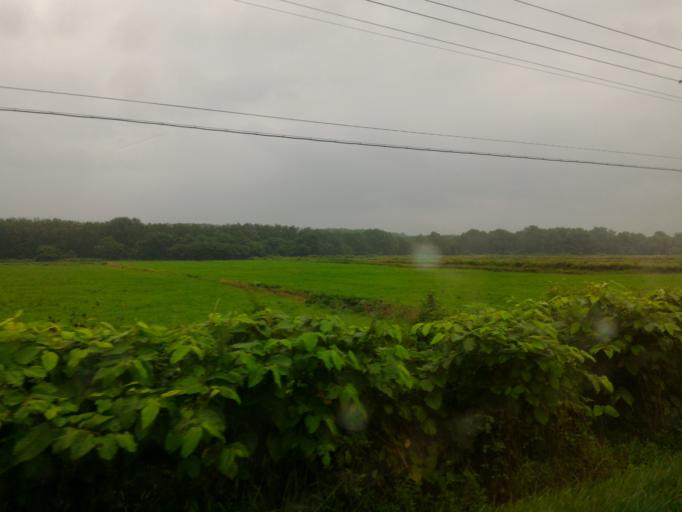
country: JP
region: Hokkaido
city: Nayoro
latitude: 44.5197
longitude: 142.3281
